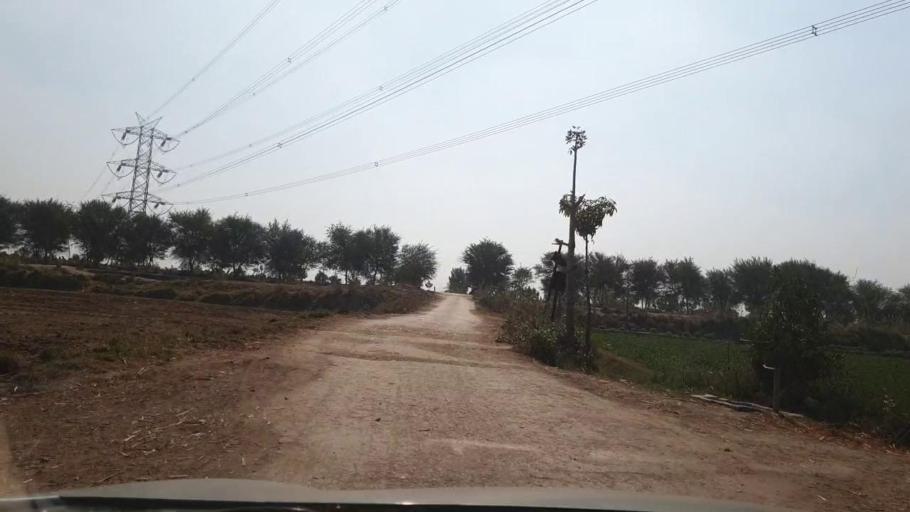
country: PK
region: Sindh
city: Tando Allahyar
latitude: 25.4742
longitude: 68.7453
